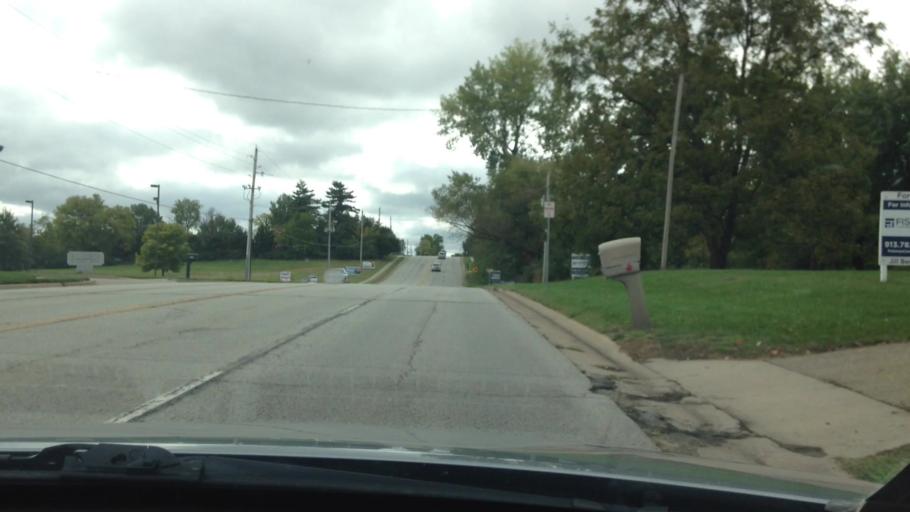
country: US
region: Kansas
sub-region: Leavenworth County
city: Lansing
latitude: 39.2724
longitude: -94.9280
